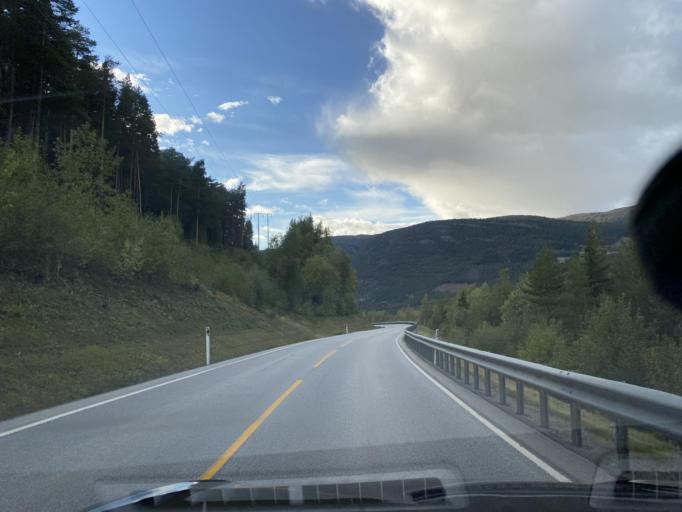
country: NO
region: Oppland
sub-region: Lom
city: Fossbergom
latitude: 61.8543
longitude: 8.6896
